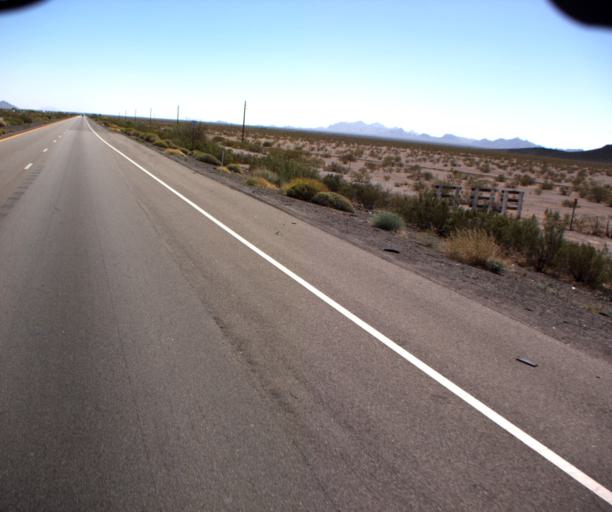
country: US
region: Arizona
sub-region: La Paz County
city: Salome
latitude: 33.6077
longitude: -113.6127
